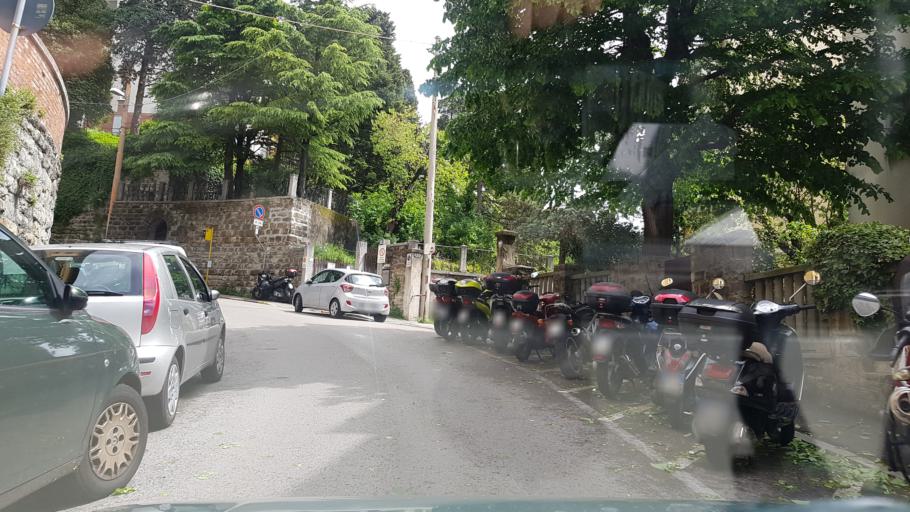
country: IT
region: Friuli Venezia Giulia
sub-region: Provincia di Trieste
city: Trieste
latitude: 45.6562
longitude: 13.7916
